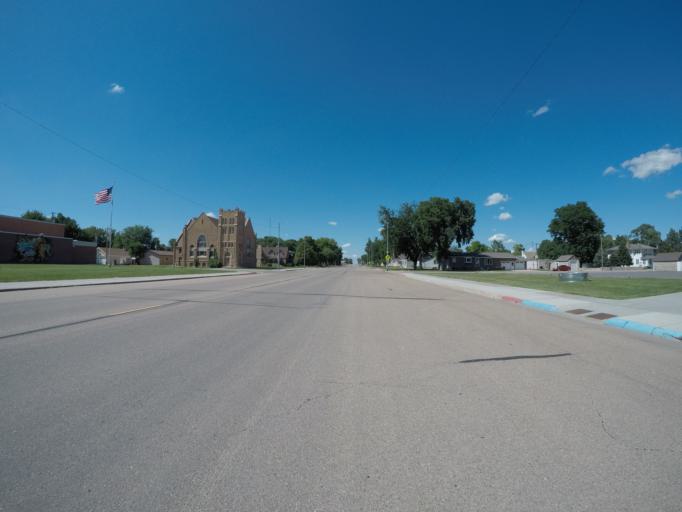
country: US
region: Nebraska
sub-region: Chase County
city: Imperial
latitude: 40.5184
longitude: -101.6431
